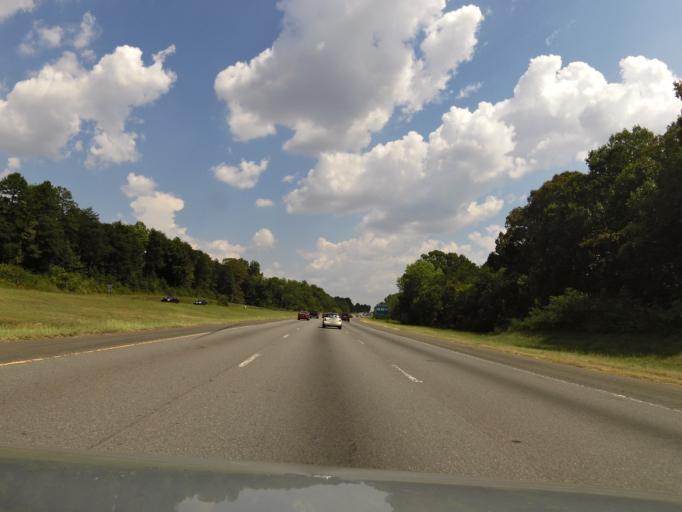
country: US
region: North Carolina
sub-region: Gaston County
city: Belmont
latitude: 35.2627
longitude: -81.0560
